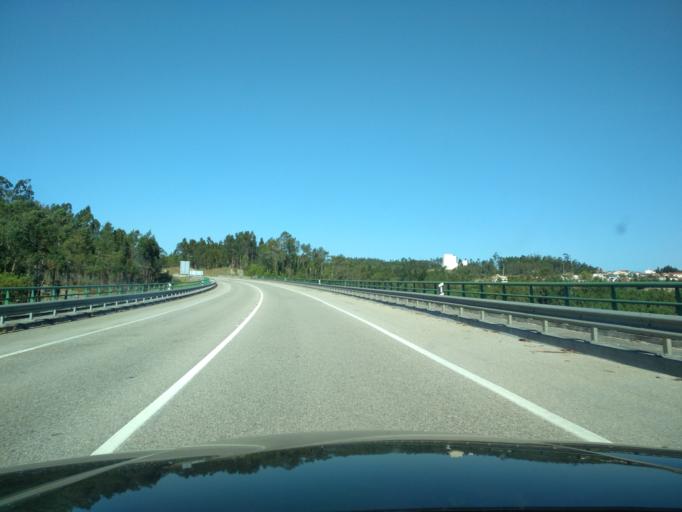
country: PT
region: Leiria
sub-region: Pombal
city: Lourical
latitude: 39.9883
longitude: -8.7383
